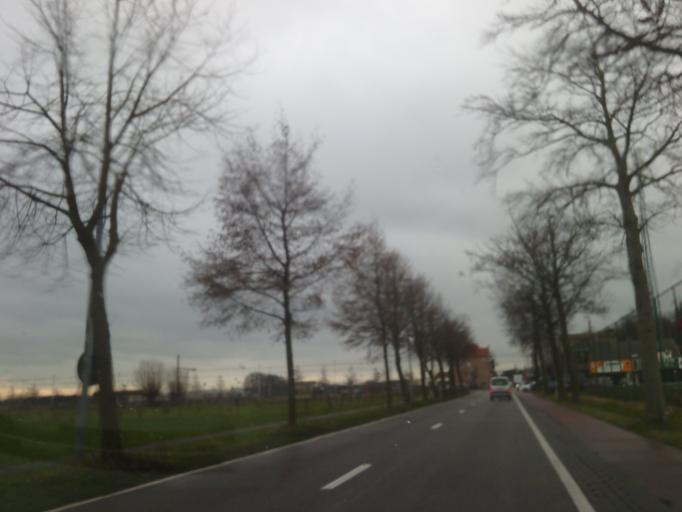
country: BE
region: Flanders
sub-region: Provincie Oost-Vlaanderen
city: Lochristi
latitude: 51.0885
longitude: 3.8793
